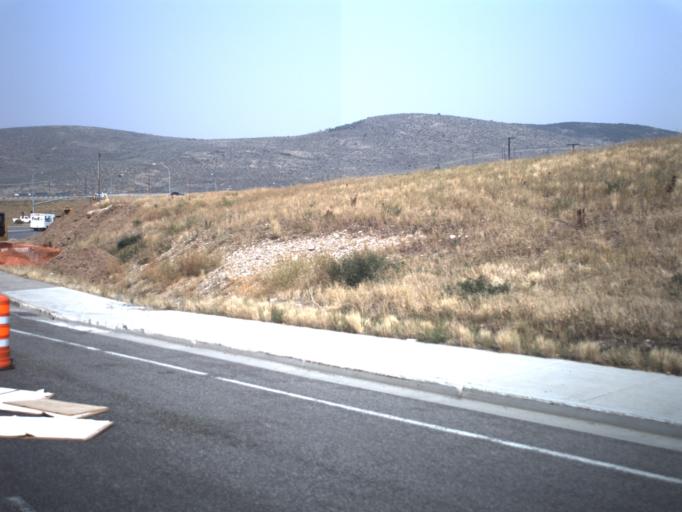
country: US
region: Utah
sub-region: Summit County
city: Park City
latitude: 40.6815
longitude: -111.4653
